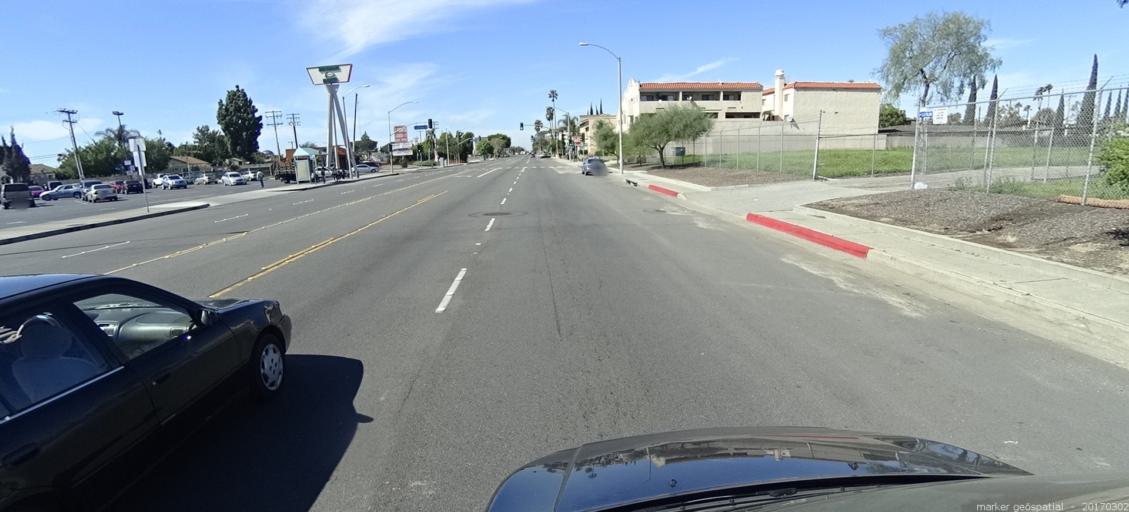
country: US
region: California
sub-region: Orange County
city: Anaheim
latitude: 33.8472
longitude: -117.9267
